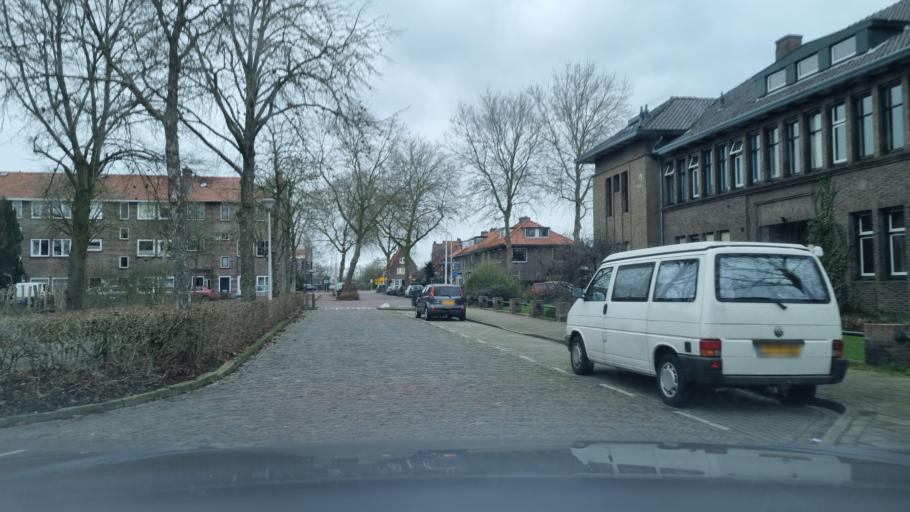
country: NL
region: Gelderland
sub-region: Gemeente Zutphen
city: Zutphen
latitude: 52.1499
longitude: 6.2096
